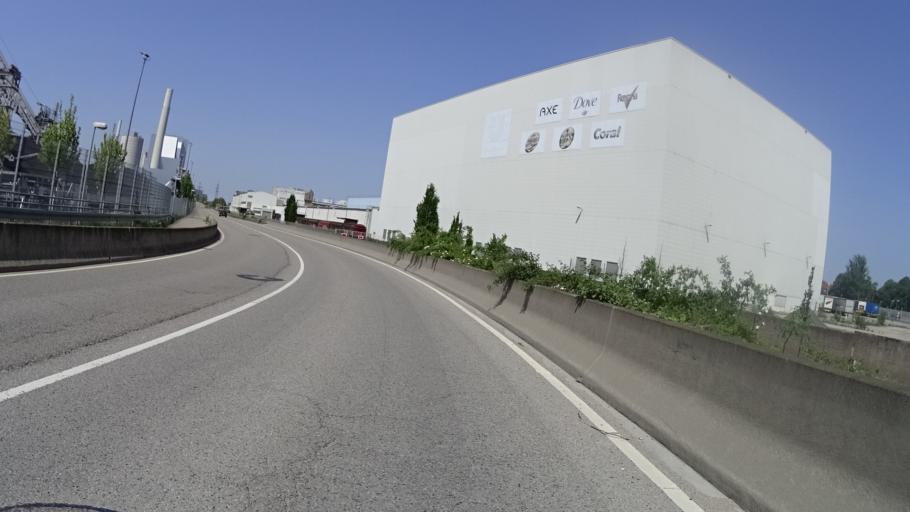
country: DE
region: Rheinland-Pfalz
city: Altrip
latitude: 49.4370
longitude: 8.5155
